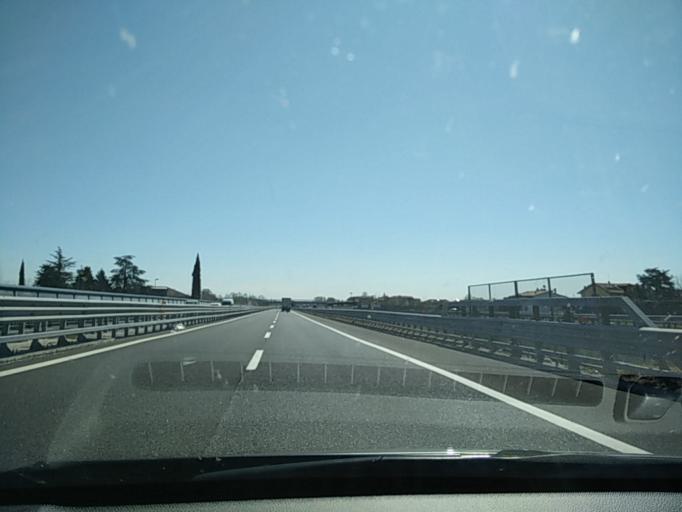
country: IT
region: Veneto
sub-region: Provincia di Padova
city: Cadoneghe
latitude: 45.4346
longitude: 11.9070
